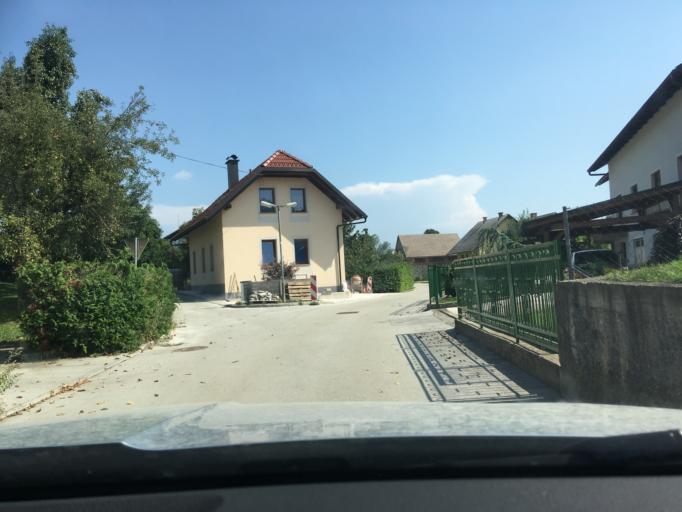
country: SI
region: Metlika
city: Metlika
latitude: 45.6525
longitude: 15.3131
